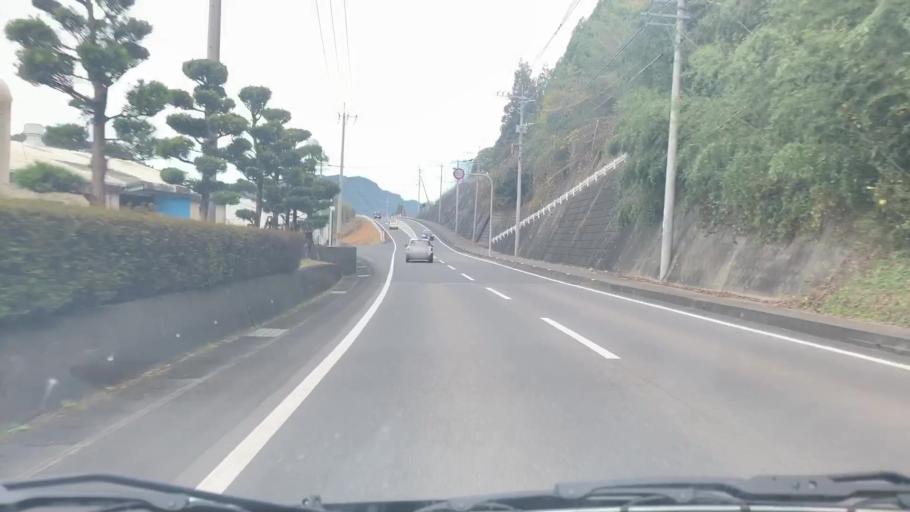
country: JP
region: Saga Prefecture
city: Imaricho-ko
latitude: 33.2891
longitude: 129.9709
